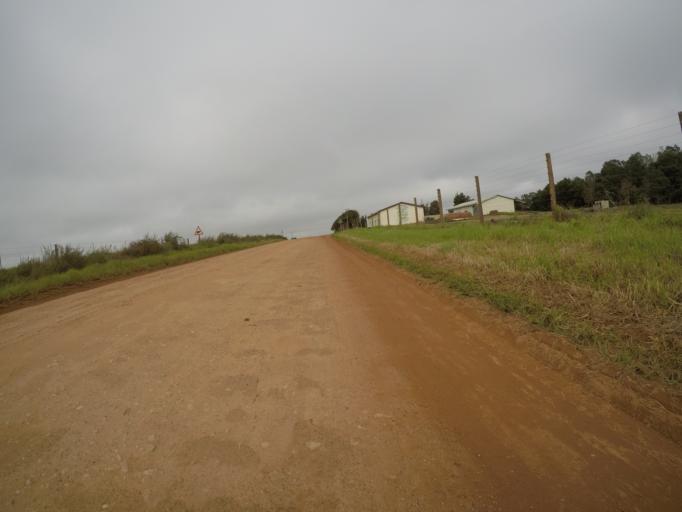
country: ZA
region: Eastern Cape
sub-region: Cacadu District Municipality
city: Kareedouw
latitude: -34.0163
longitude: 24.2384
